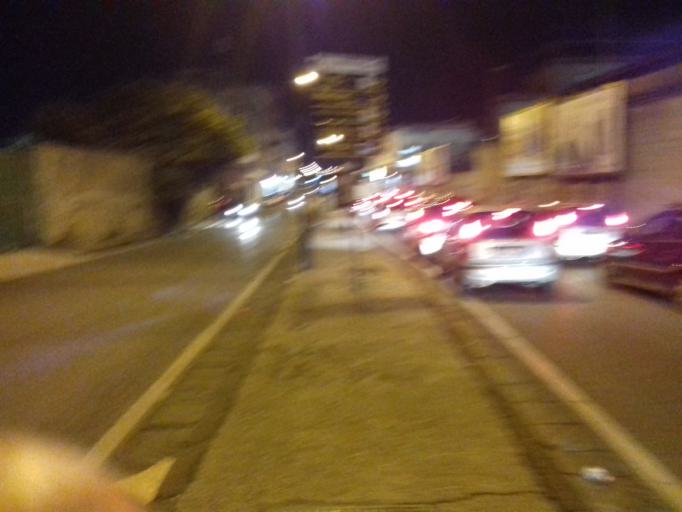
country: IT
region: Campania
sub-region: Provincia di Napoli
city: Napoli
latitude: 40.8558
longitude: 14.2864
